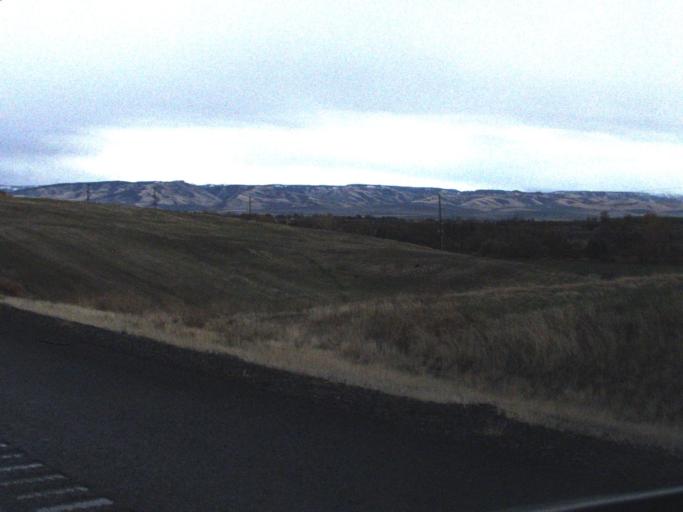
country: US
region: Washington
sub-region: Walla Walla County
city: Garrett
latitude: 46.0565
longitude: -118.4437
